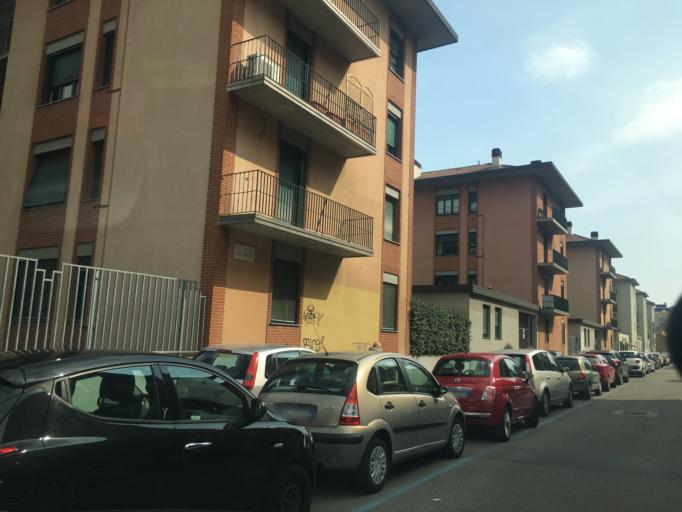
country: IT
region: Lombardy
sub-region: Citta metropolitana di Milano
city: Bresso
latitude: 45.5246
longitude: 9.2055
